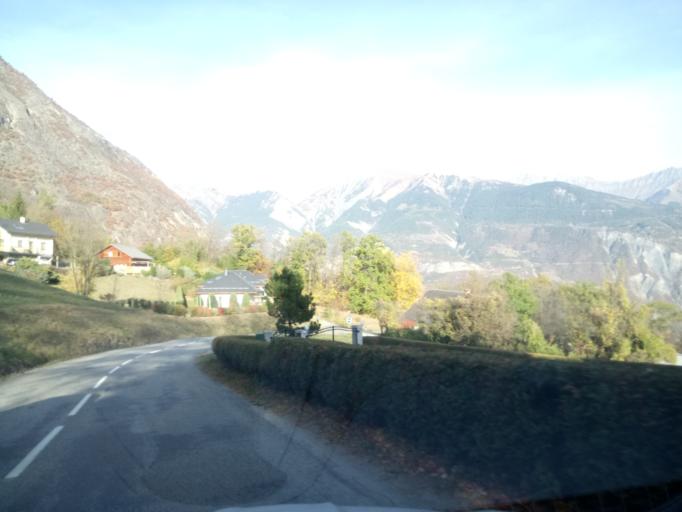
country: FR
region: Rhone-Alpes
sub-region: Departement de la Savoie
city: Saint-Jean-de-Maurienne
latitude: 45.2753
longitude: 6.3287
